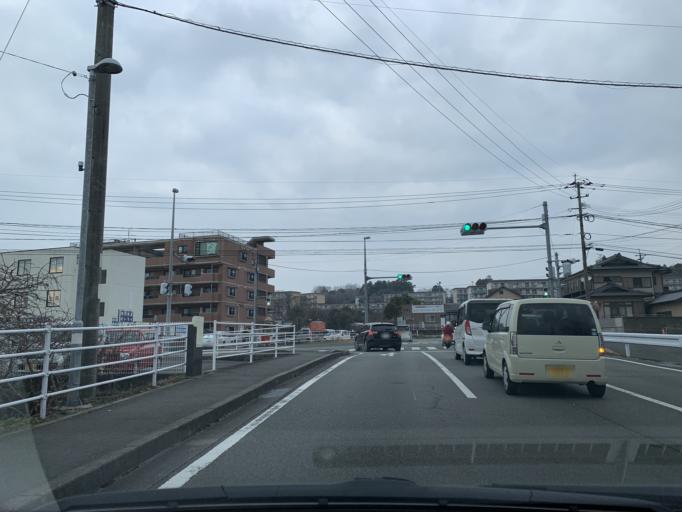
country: JP
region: Kumamoto
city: Ozu
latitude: 32.8775
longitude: 130.8578
